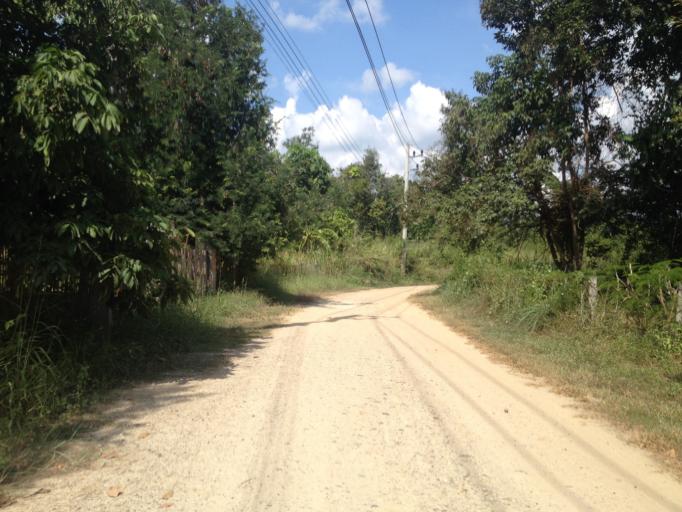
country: TH
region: Chiang Mai
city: Hang Dong
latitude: 18.7019
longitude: 98.8694
